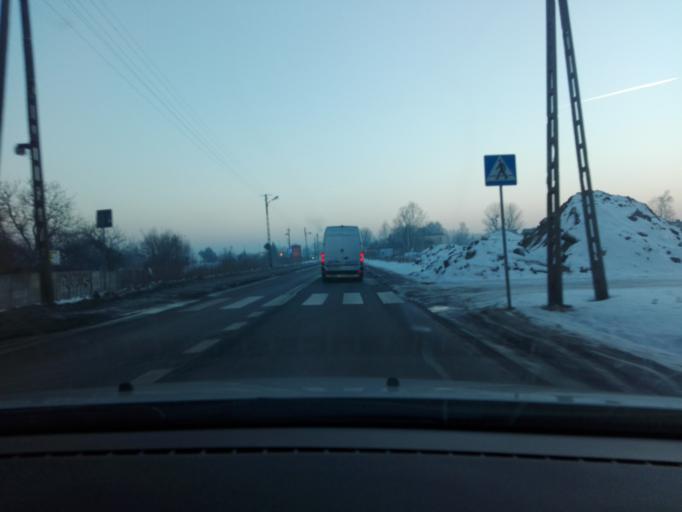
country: PL
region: Lodz Voivodeship
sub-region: Powiat zgierski
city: Zgierz
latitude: 51.8750
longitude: 19.4095
